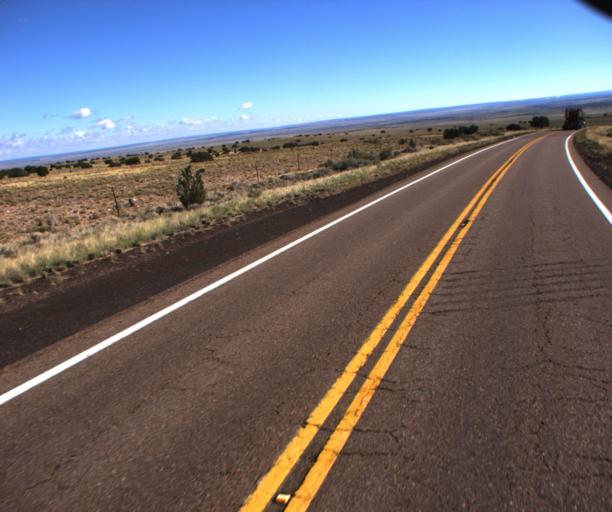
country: US
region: Arizona
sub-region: Apache County
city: Saint Johns
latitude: 34.4990
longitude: -109.5027
